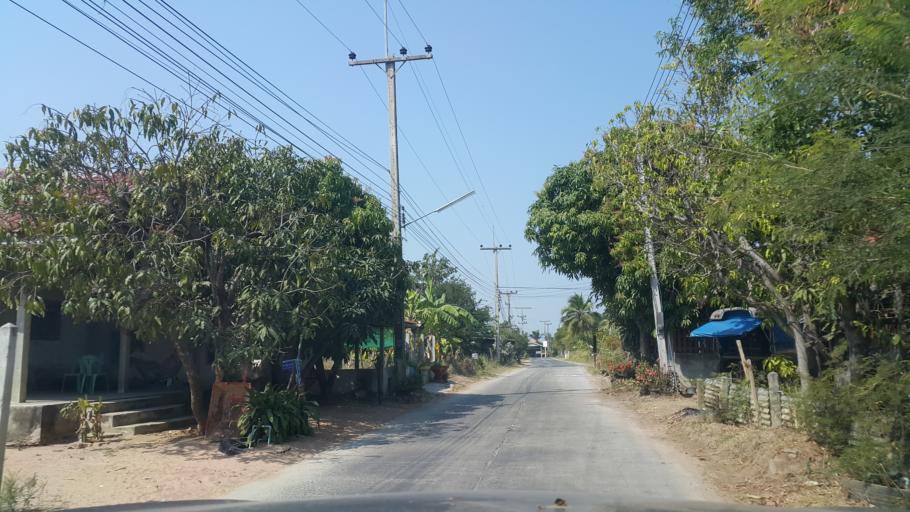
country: TH
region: Buriram
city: Satuek
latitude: 15.1476
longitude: 103.3334
